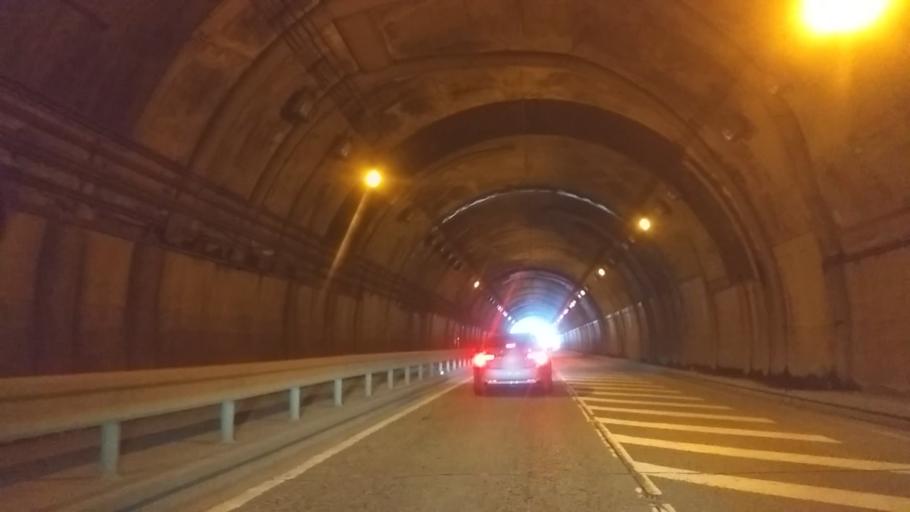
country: JP
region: Shizuoka
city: Gotemba
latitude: 35.3678
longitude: 139.0200
